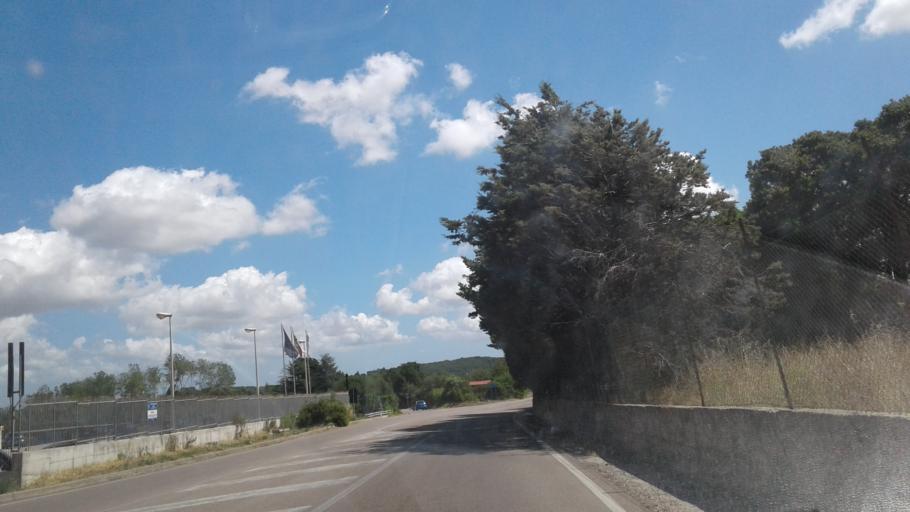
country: IT
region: Sardinia
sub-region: Provincia di Olbia-Tempio
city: Tempio Pausania
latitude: 40.9059
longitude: 9.1268
